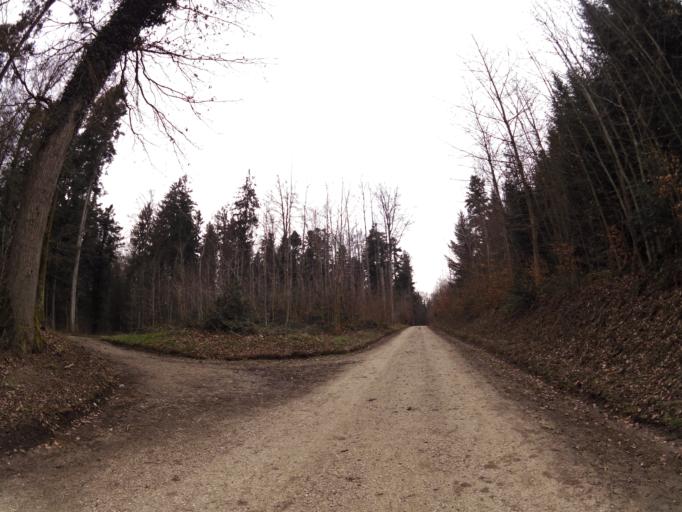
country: CH
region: Aargau
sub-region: Bezirk Aarau
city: Aarau
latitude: 47.3767
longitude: 8.0341
